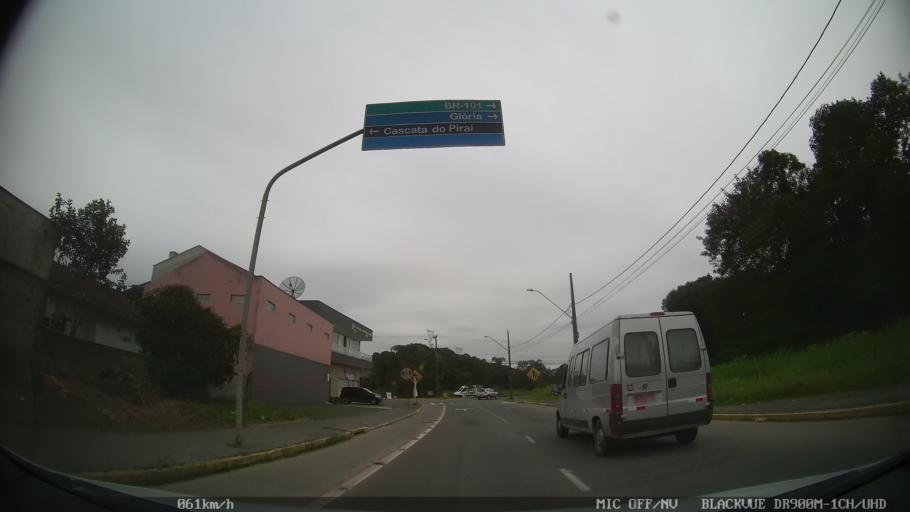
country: BR
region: Santa Catarina
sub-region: Joinville
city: Joinville
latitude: -26.2909
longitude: -48.8925
